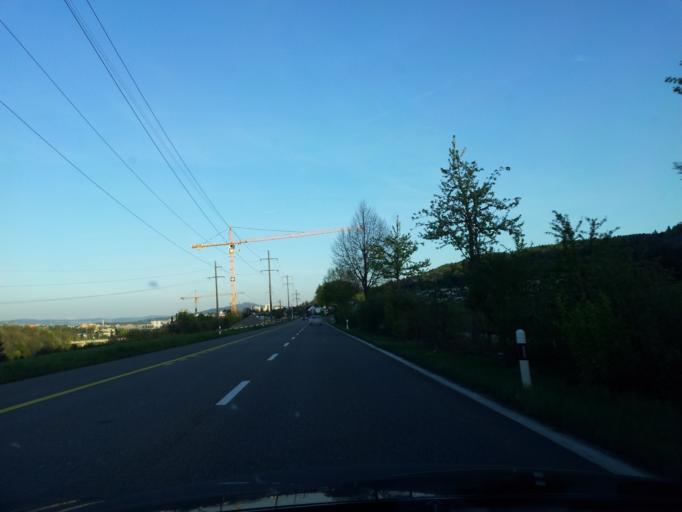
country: CH
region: Aargau
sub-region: Bezirk Baden
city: Killwangen
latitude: 47.4398
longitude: 8.3393
